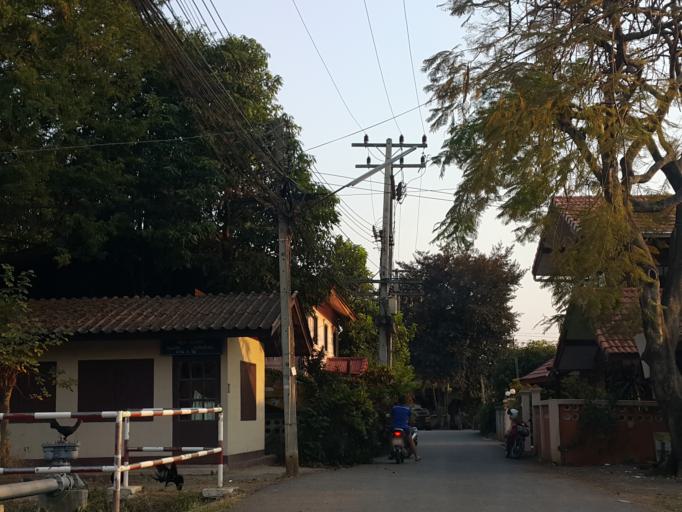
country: TH
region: Chiang Mai
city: San Sai
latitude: 18.9017
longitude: 98.9547
